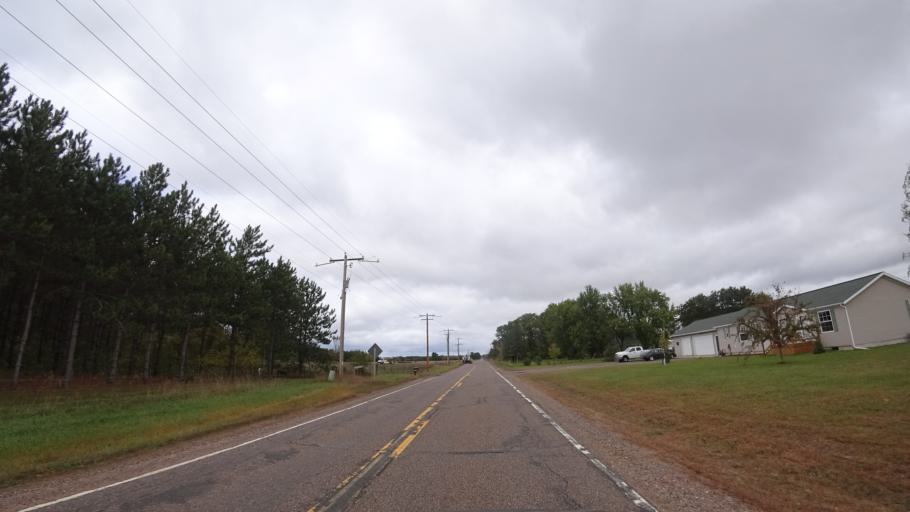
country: US
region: Wisconsin
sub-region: Chippewa County
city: Lake Wissota
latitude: 44.9609
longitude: -91.2678
